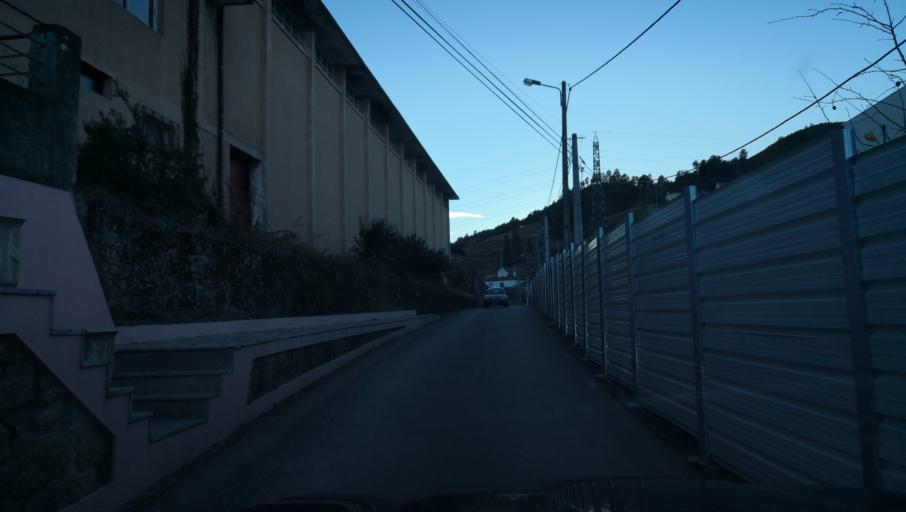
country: PT
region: Vila Real
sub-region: Vila Real
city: Vila Real
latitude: 41.2568
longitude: -7.7683
